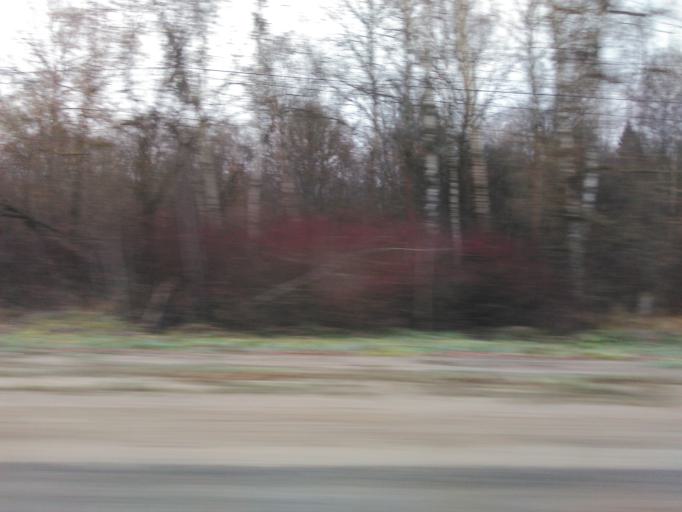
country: RU
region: Moskovskaya
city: Ashukino
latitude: 56.1492
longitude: 37.9881
